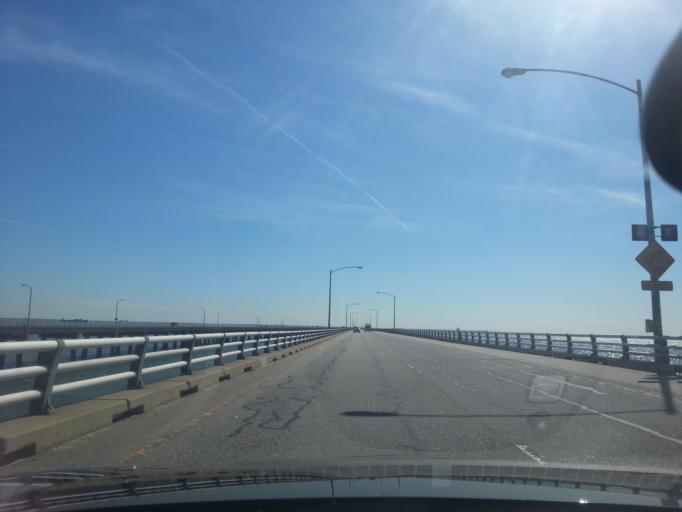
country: US
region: Virginia
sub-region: City of Virginia Beach
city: Virginia Beach
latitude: 37.0072
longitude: -76.0966
